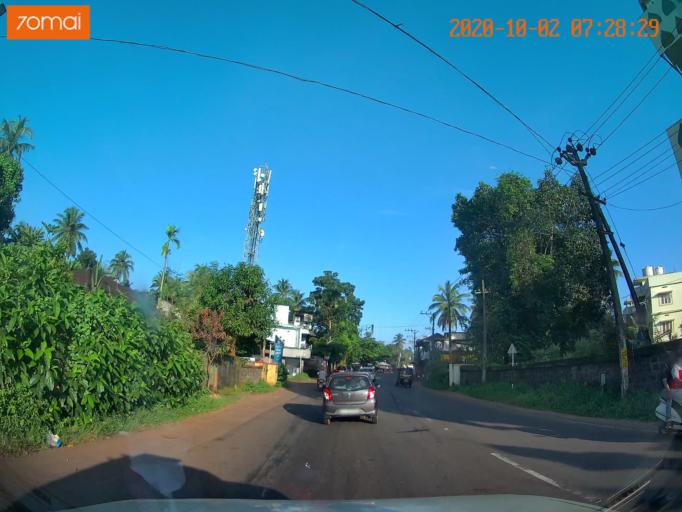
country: IN
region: Kerala
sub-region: Malappuram
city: Pariyapuram
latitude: 11.0288
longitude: 75.9428
